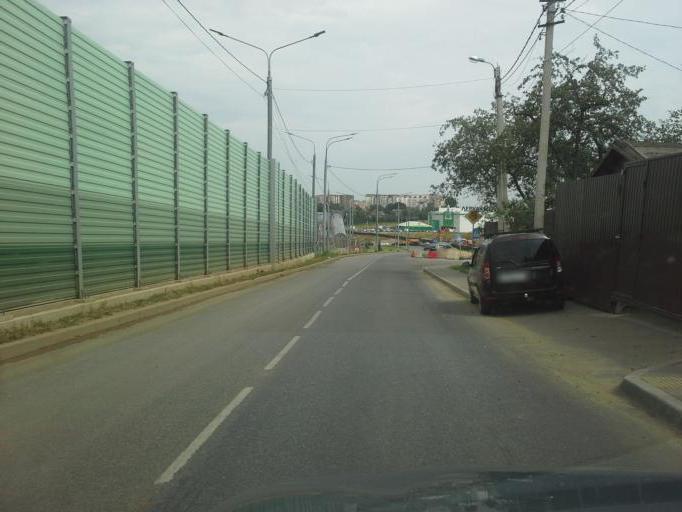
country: RU
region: Moskovskaya
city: Lesnoy Gorodok
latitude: 55.6561
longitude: 37.1737
